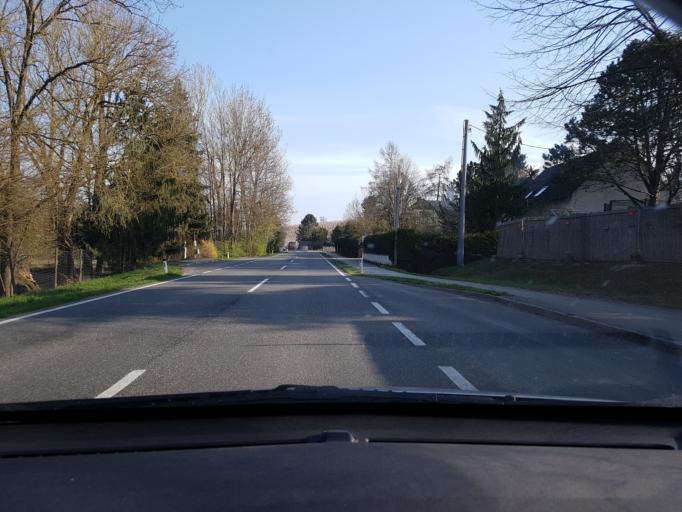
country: AT
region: Upper Austria
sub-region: Politischer Bezirk Linz-Land
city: Sankt Florian
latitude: 48.1691
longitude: 14.3432
